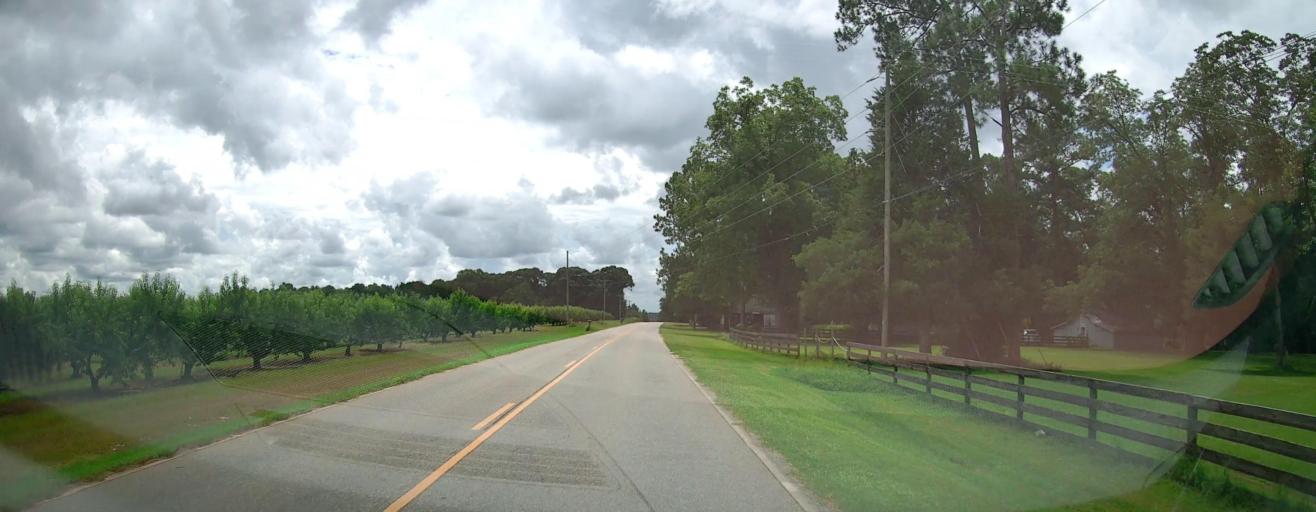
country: US
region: Georgia
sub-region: Peach County
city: Byron
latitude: 32.5577
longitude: -83.7533
